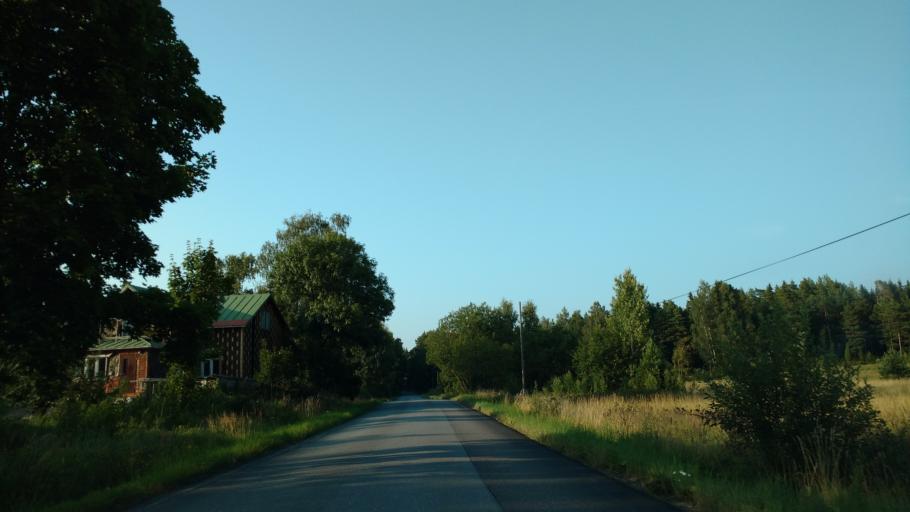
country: FI
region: Varsinais-Suomi
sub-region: Aboland-Turunmaa
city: Dragsfjaerd
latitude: 59.9713
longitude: 22.4471
